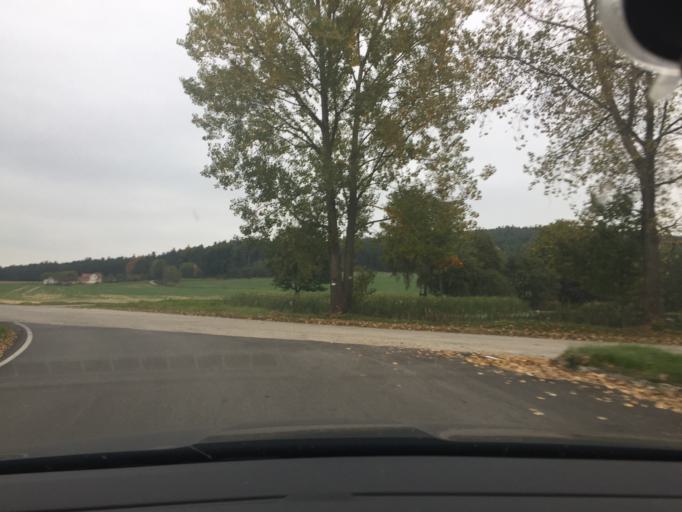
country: CZ
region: Jihocesky
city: Brloh
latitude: 48.9500
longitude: 14.2642
